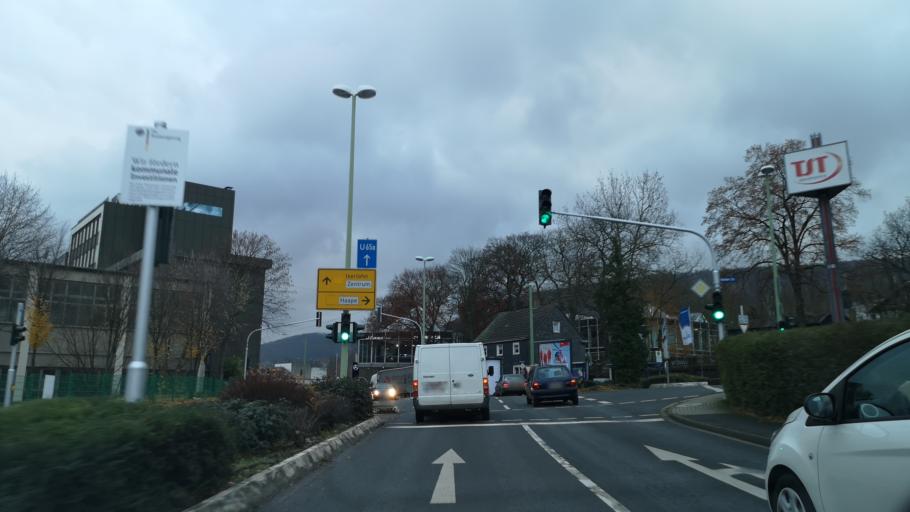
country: DE
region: North Rhine-Westphalia
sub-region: Regierungsbezirk Arnsberg
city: Hagen
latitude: 51.3506
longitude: 7.4385
